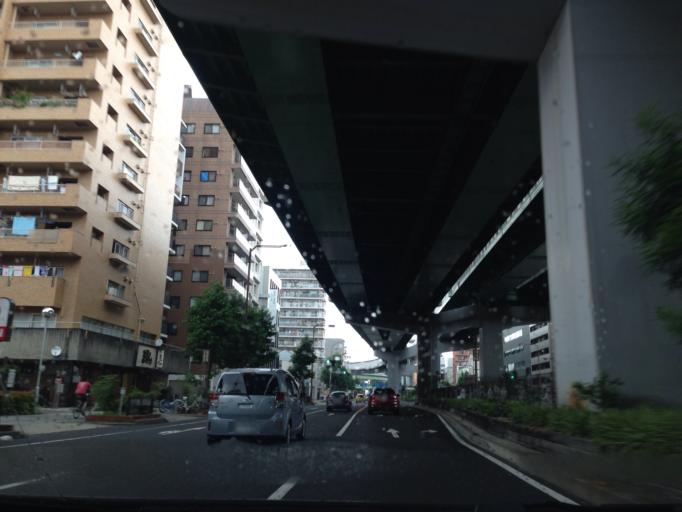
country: JP
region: Aichi
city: Nagoya-shi
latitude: 35.1752
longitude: 136.9144
